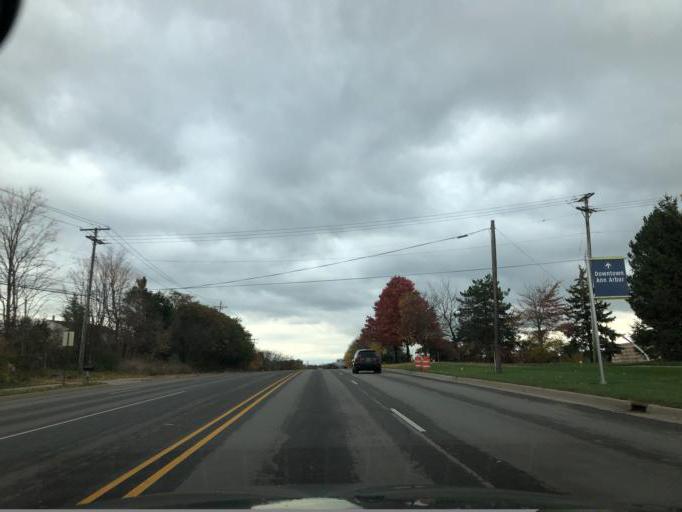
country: US
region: Michigan
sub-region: Washtenaw County
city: Ann Arbor
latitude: 42.2482
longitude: -83.7602
